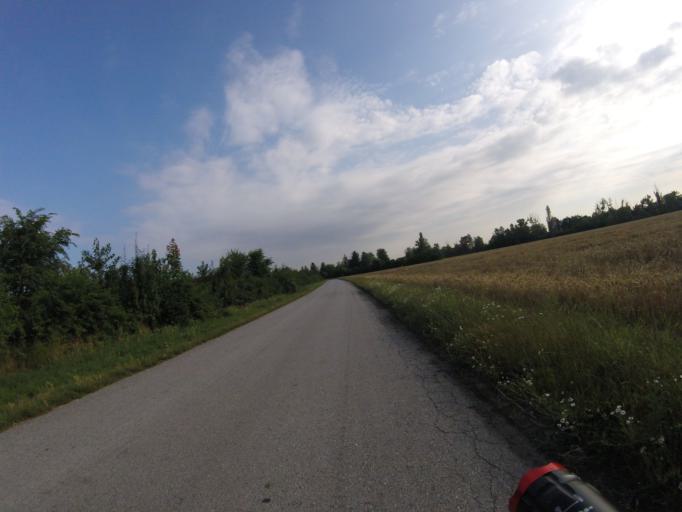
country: AT
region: Lower Austria
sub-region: Politischer Bezirk Baden
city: Trumau
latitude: 48.0289
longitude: 16.3462
